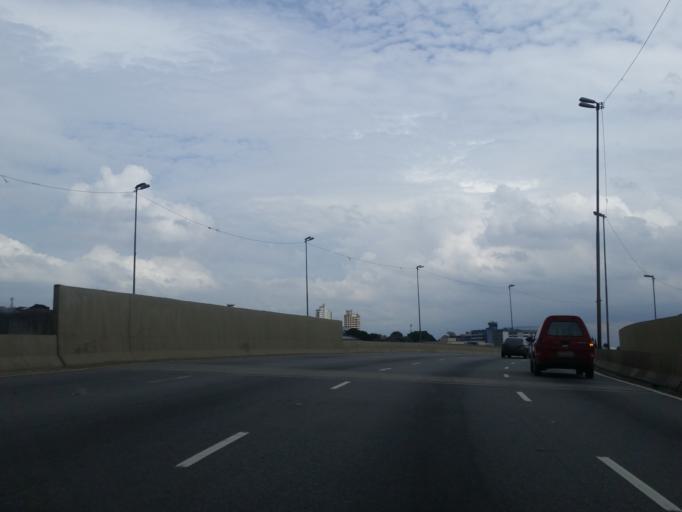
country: BR
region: Sao Paulo
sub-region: Guarulhos
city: Guarulhos
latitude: -23.4914
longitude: -46.4528
